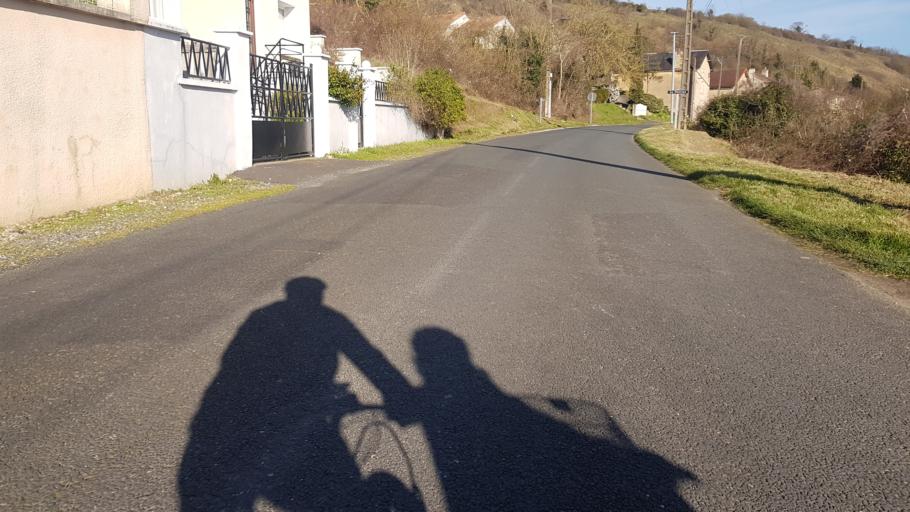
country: FR
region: Poitou-Charentes
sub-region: Departement de la Vienne
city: Migne-Auxances
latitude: 46.6426
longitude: 0.3411
